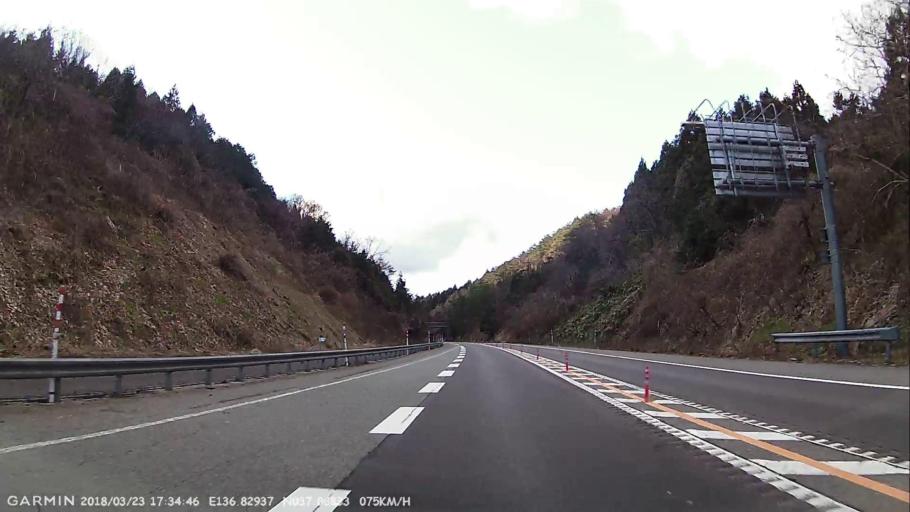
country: JP
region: Ishikawa
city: Nanao
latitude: 37.0684
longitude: 136.8293
